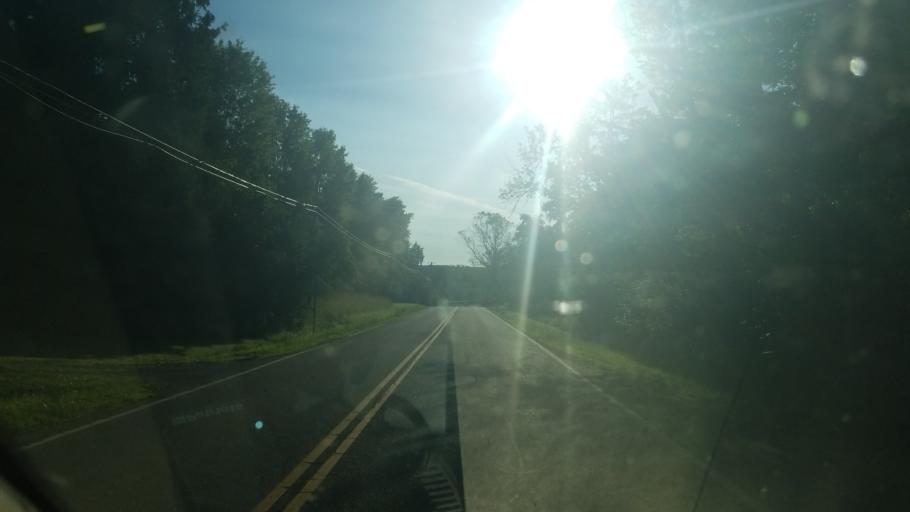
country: US
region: Ohio
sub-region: Columbiana County
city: Salem
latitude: 40.8914
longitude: -80.8898
